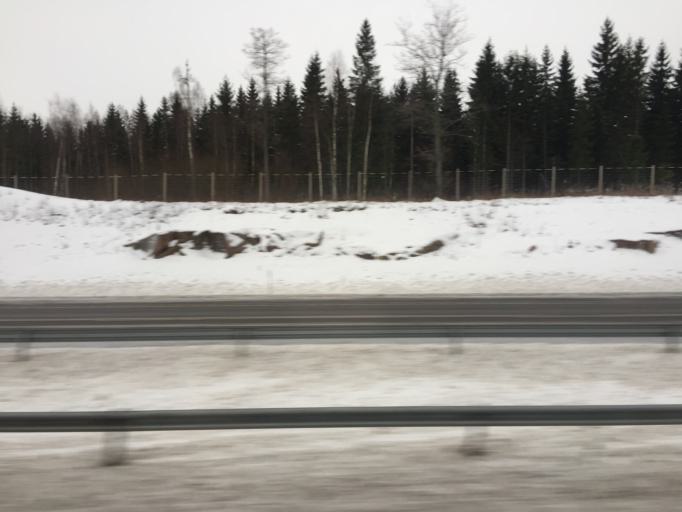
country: FI
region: Kymenlaakso
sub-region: Kotka-Hamina
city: Broby
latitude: 60.5012
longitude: 26.8105
